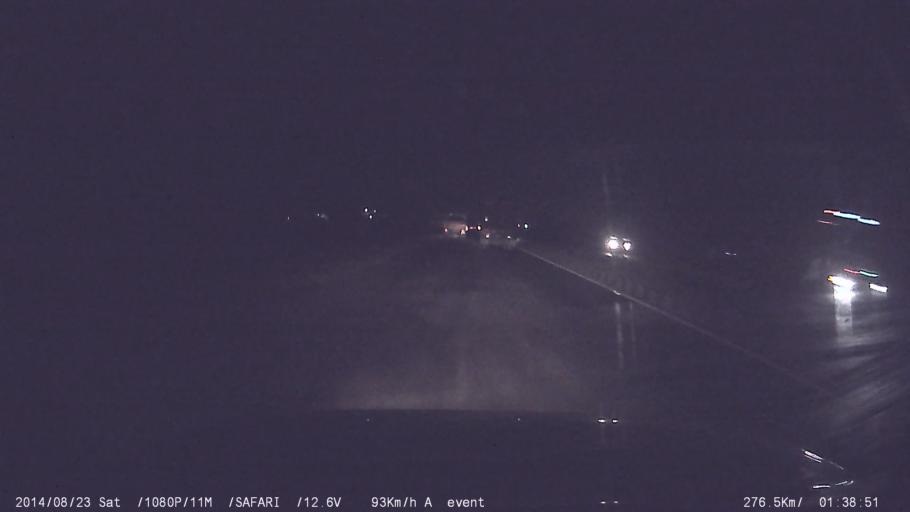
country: IN
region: Tamil Nadu
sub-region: Kancheepuram
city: Wallajahbad
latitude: 12.9015
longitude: 79.8130
